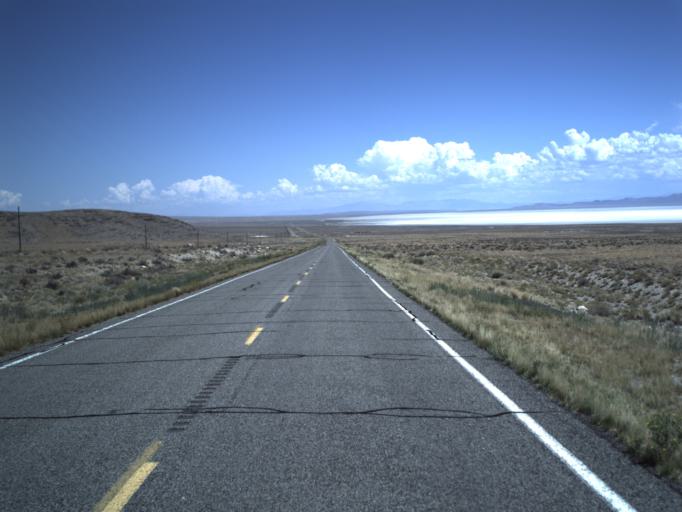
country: US
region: Utah
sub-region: Beaver County
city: Milford
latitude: 39.0512
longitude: -113.2705
